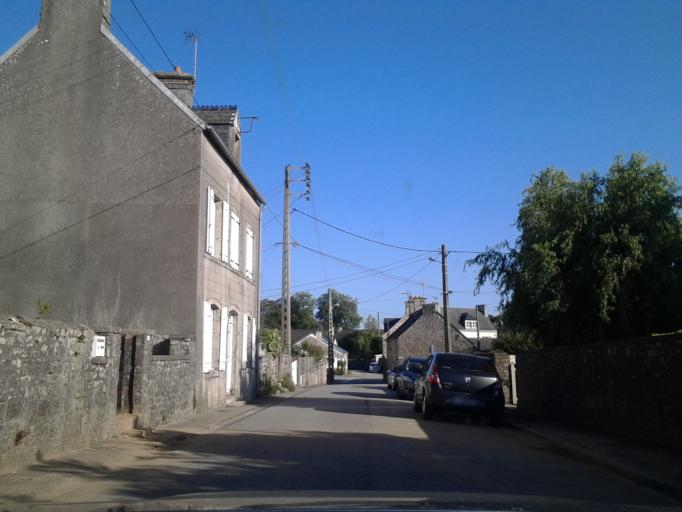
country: FR
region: Lower Normandy
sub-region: Departement de la Manche
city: Valognes
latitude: 49.5132
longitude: -1.4729
